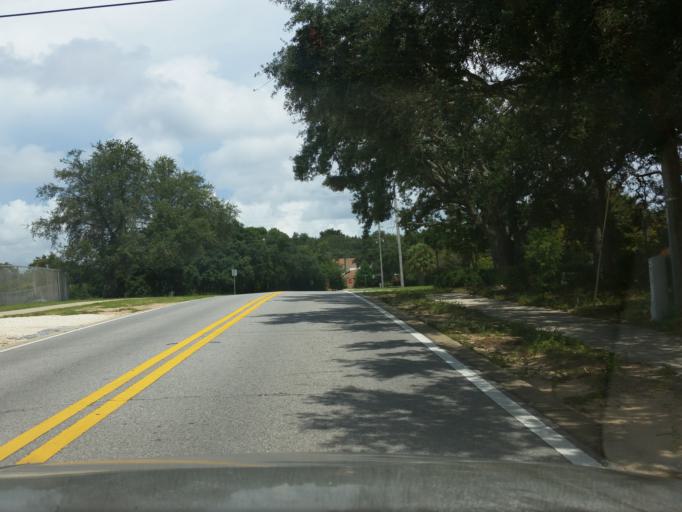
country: US
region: Florida
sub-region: Santa Rosa County
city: Gulf Breeze
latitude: 30.3628
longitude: -87.1662
